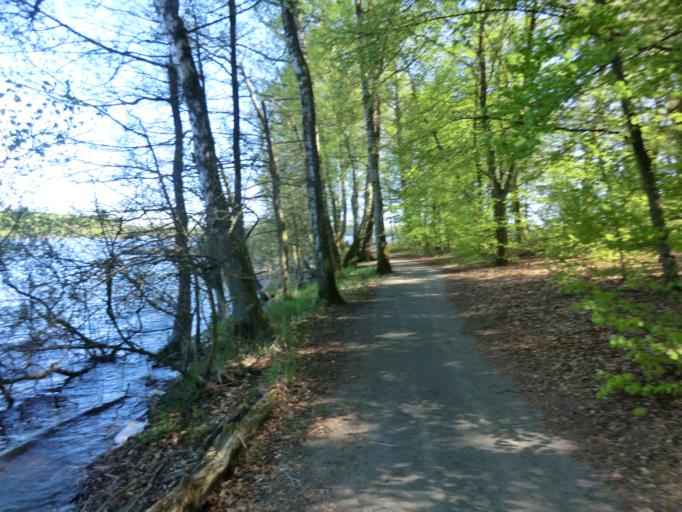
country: SE
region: Skane
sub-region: Sjobo Kommun
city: Sjoebo
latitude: 55.5682
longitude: 13.7192
